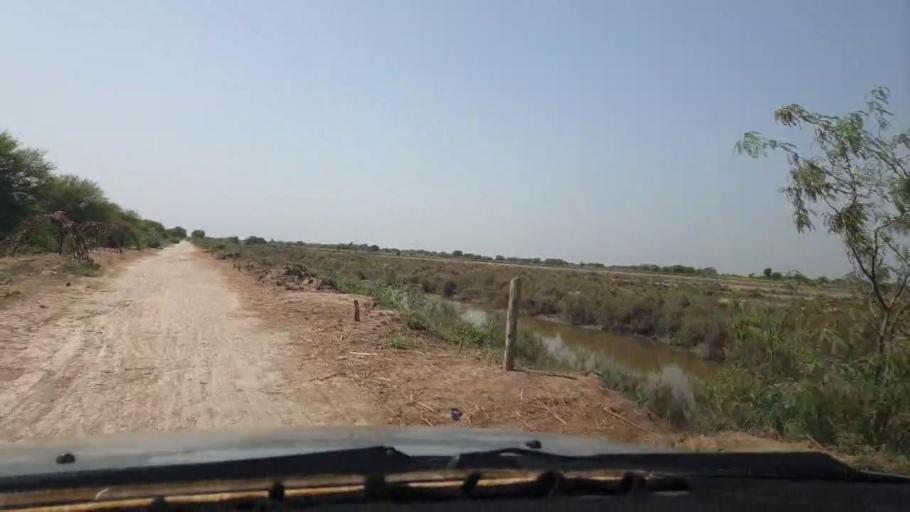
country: PK
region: Sindh
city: Tando Ghulam Ali
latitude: 25.1431
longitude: 68.8037
